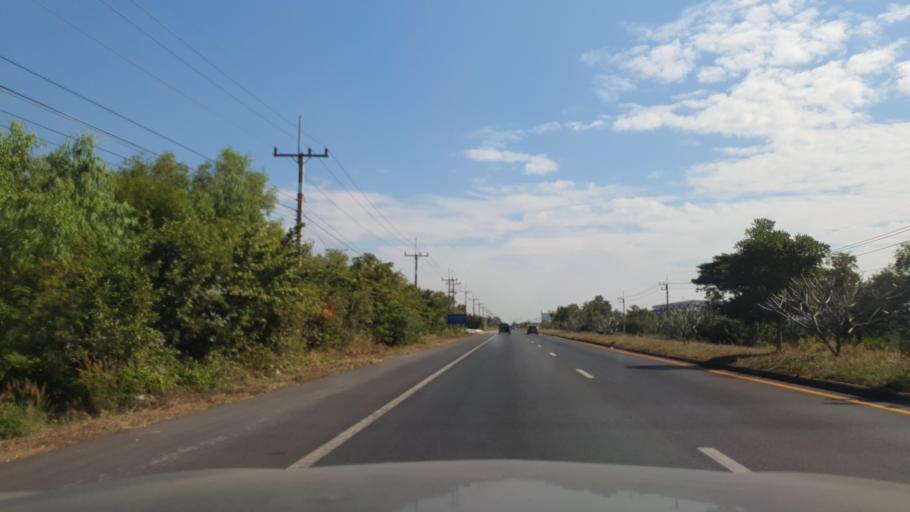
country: TH
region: Maha Sarakham
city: Kantharawichai
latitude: 16.3820
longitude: 103.2114
